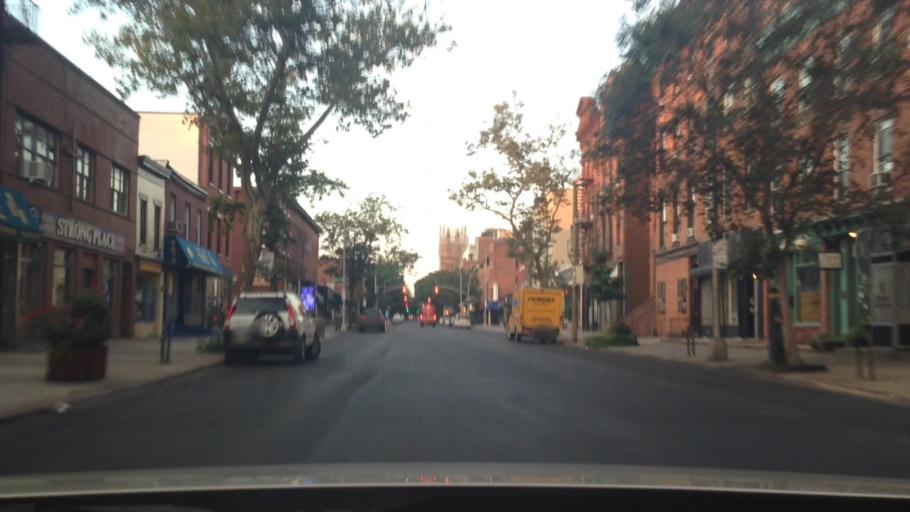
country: US
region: New York
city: New York City
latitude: 40.6849
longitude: -73.9947
